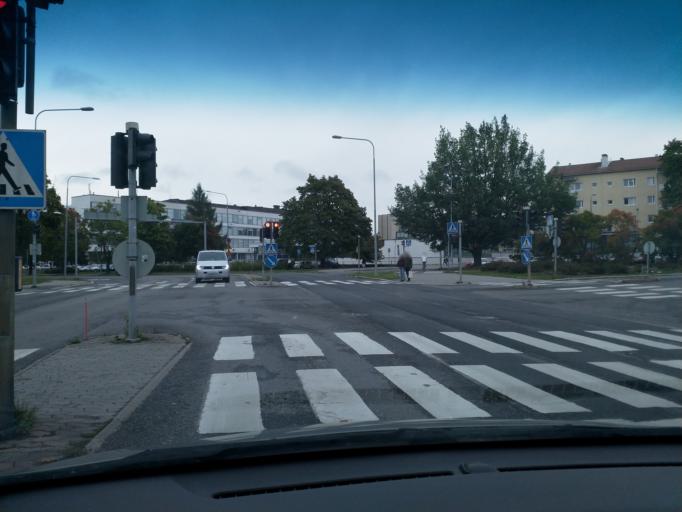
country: FI
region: Pirkanmaa
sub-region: Tampere
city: Tampere
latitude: 61.4970
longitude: 23.7864
